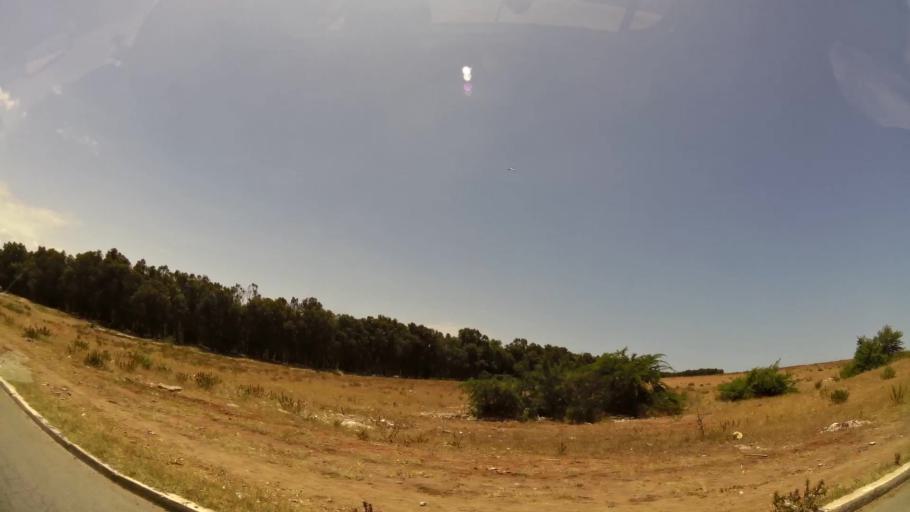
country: MA
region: Gharb-Chrarda-Beni Hssen
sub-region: Kenitra Province
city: Kenitra
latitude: 34.2483
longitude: -6.6230
